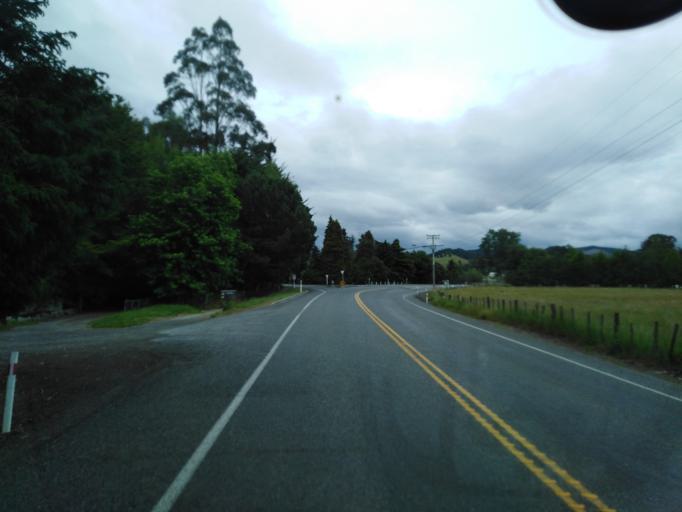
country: NZ
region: Tasman
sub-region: Tasman District
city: Wakefield
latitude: -41.4537
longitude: 172.9570
